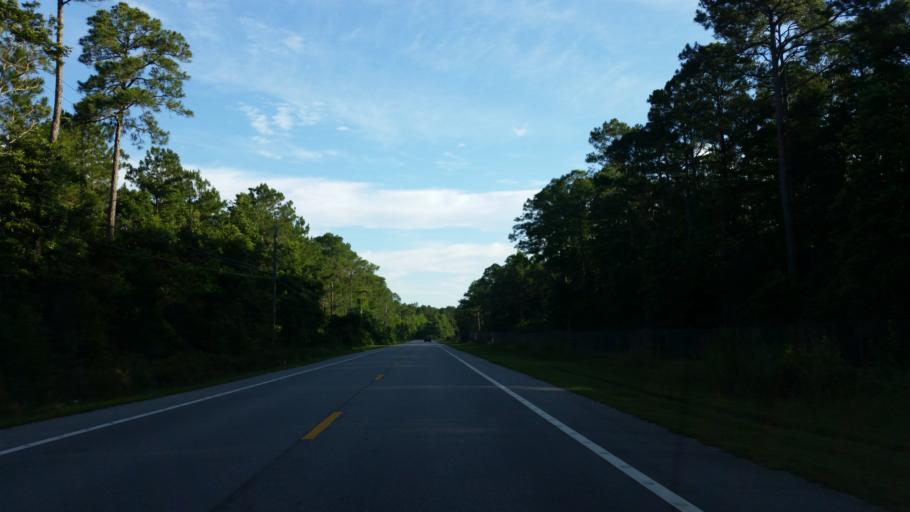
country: US
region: Florida
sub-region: Escambia County
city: Warrington
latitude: 30.3465
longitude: -87.3428
